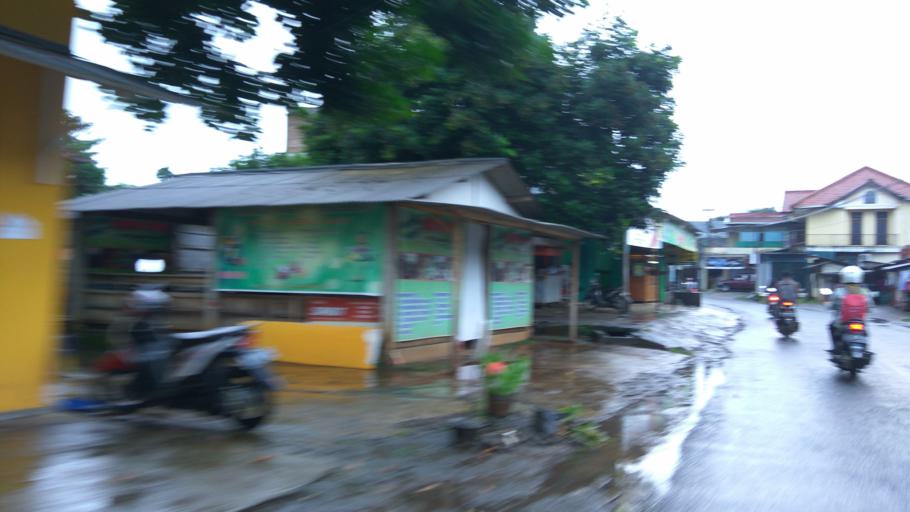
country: ID
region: Central Java
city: Semarang
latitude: -7.0591
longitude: 110.3971
